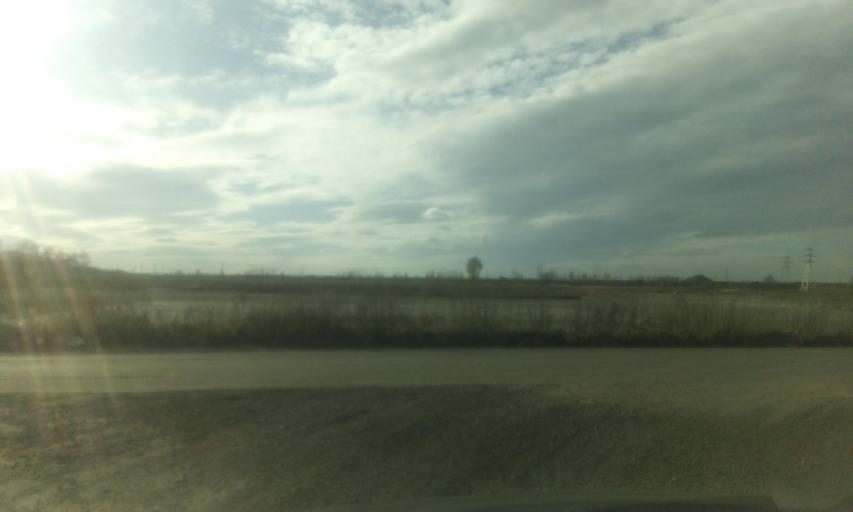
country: RU
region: Tula
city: Dubovka
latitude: 53.9396
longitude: 38.0298
